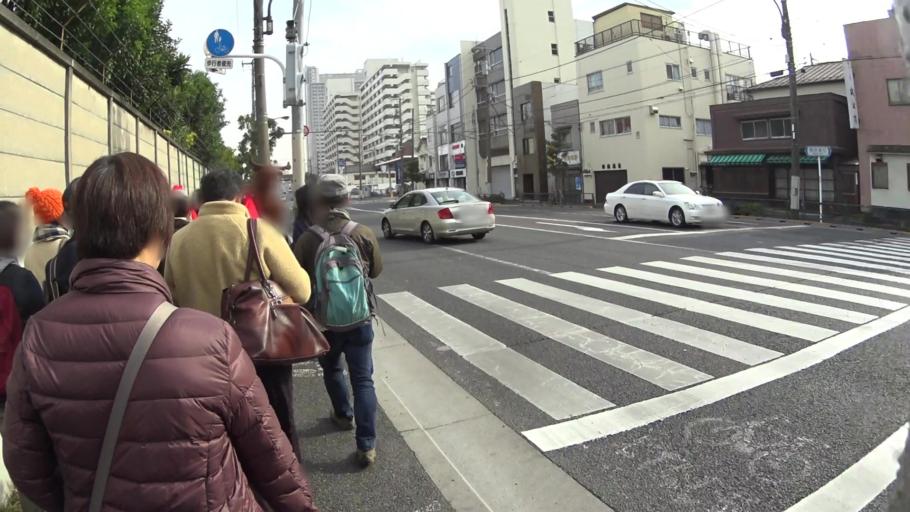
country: JP
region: Saitama
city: Soka
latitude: 35.7279
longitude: 139.8054
